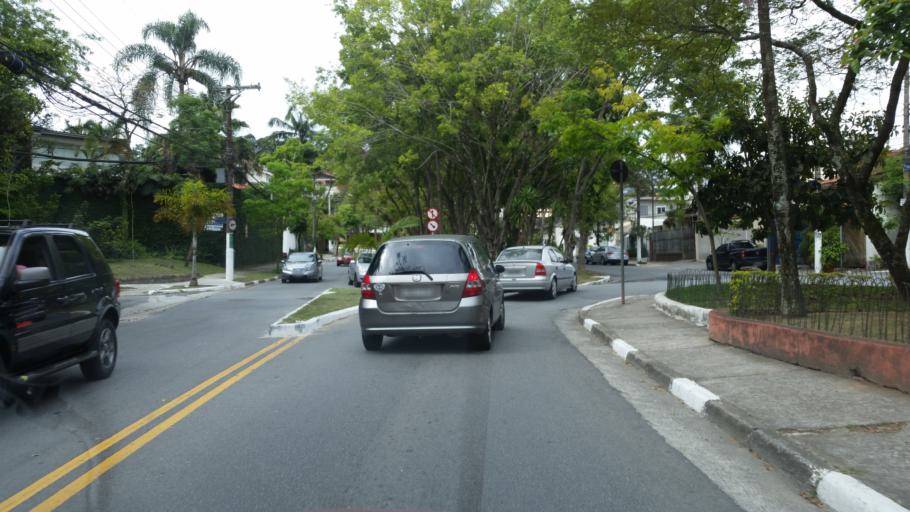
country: BR
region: Sao Paulo
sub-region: Diadema
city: Diadema
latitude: -23.6570
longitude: -46.6831
